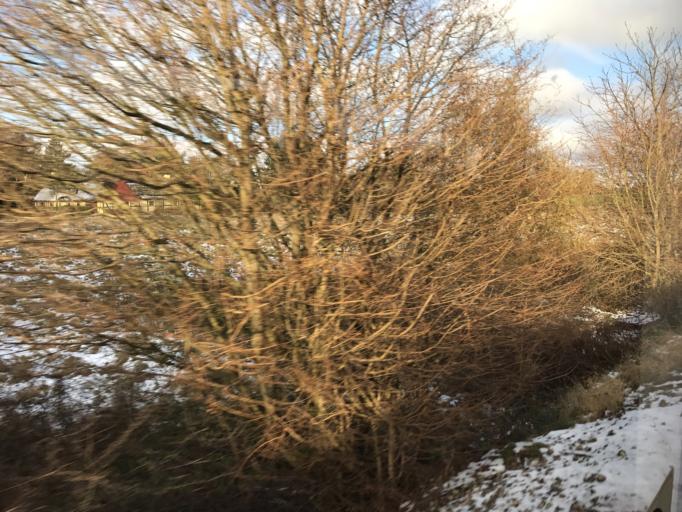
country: DK
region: Zealand
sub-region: Stevns Kommune
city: Stroby Egede
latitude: 55.4015
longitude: 12.1922
